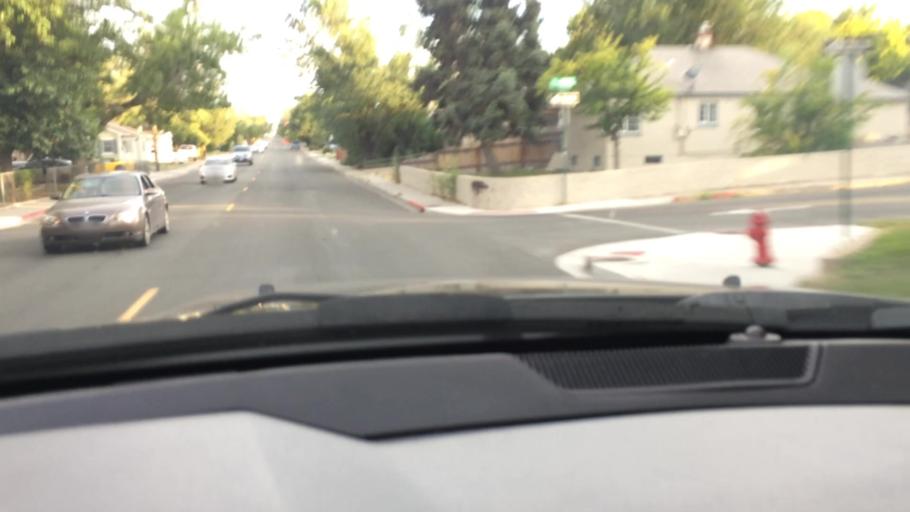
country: US
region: Nevada
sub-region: Washoe County
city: Reno
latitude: 39.5117
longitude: -119.8127
